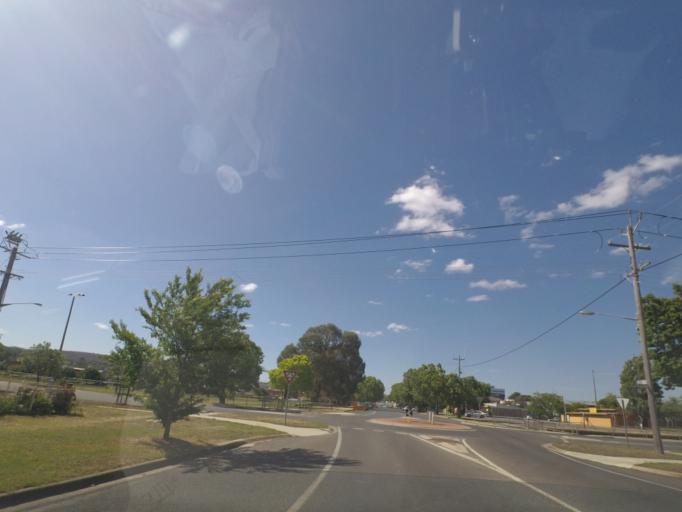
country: AU
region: New South Wales
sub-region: Albury Municipality
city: South Albury
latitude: -36.0872
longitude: 146.9144
